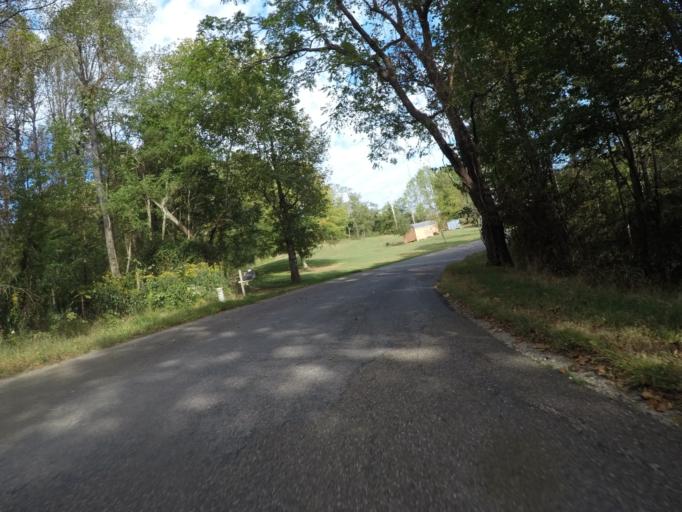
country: US
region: West Virginia
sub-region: Cabell County
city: Lesage
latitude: 38.5716
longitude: -82.4305
